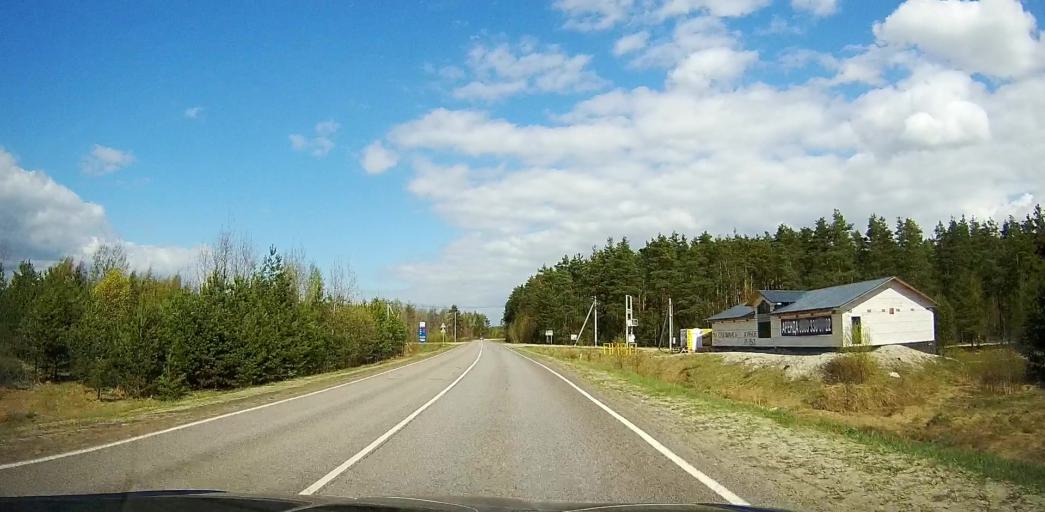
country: RU
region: Moskovskaya
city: Davydovo
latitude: 55.5490
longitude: 38.8169
